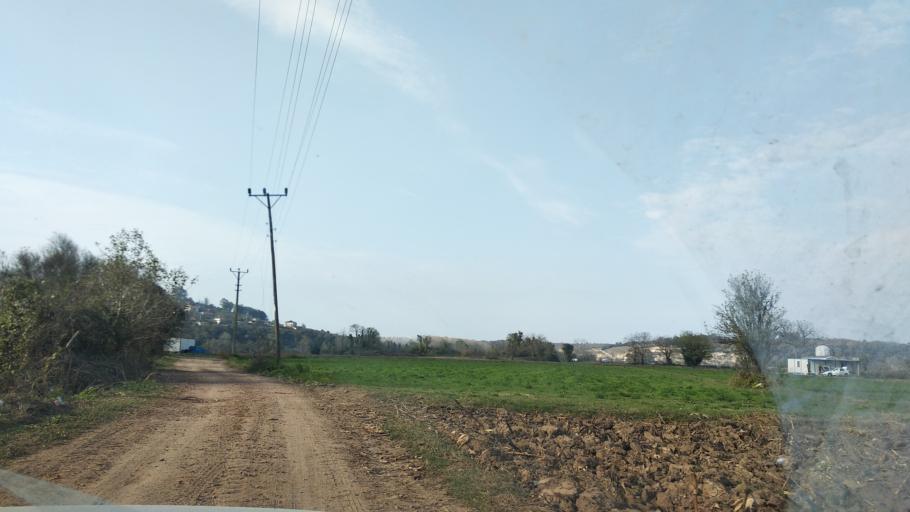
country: TR
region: Sakarya
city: Karasu
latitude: 41.0871
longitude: 30.6003
